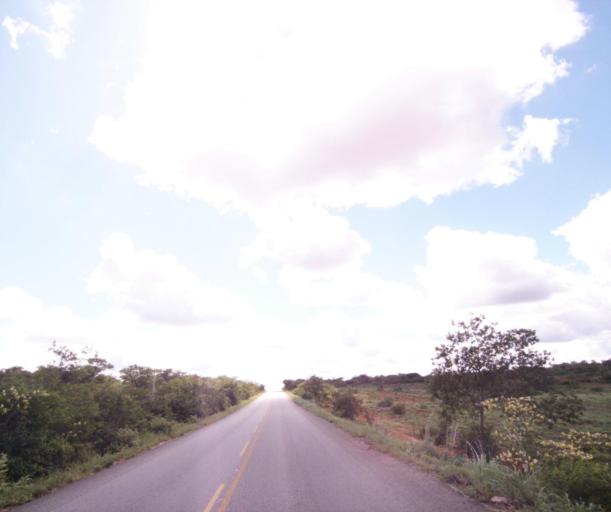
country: BR
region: Bahia
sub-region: Caetite
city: Caetite
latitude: -14.1675
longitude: -42.2420
